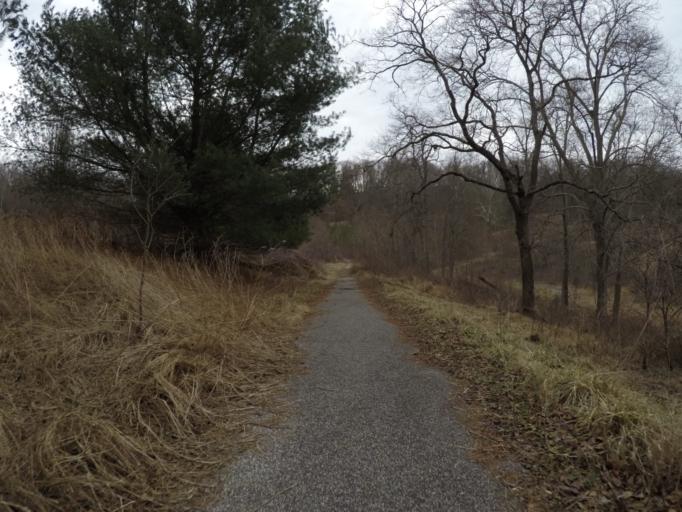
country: US
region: Ohio
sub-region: Lawrence County
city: Burlington
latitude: 38.3827
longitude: -82.5095
